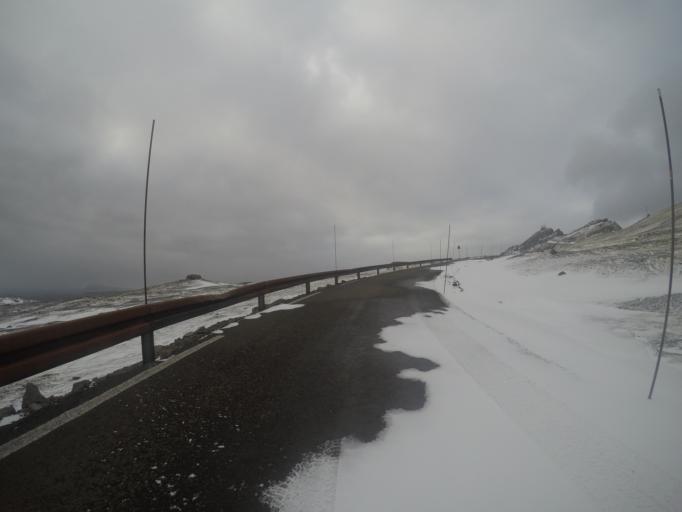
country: FO
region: Streymoy
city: Kollafjordhur
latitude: 62.0785
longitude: -6.9567
